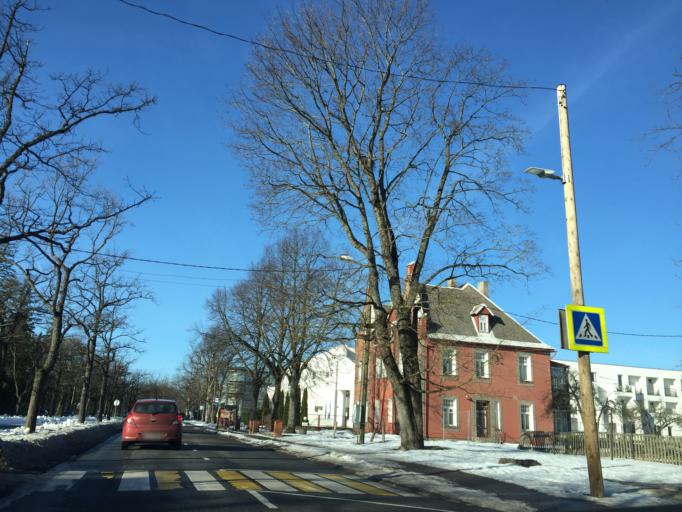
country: EE
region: Paernumaa
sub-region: Paernu linn
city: Parnu
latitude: 58.3767
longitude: 24.5035
